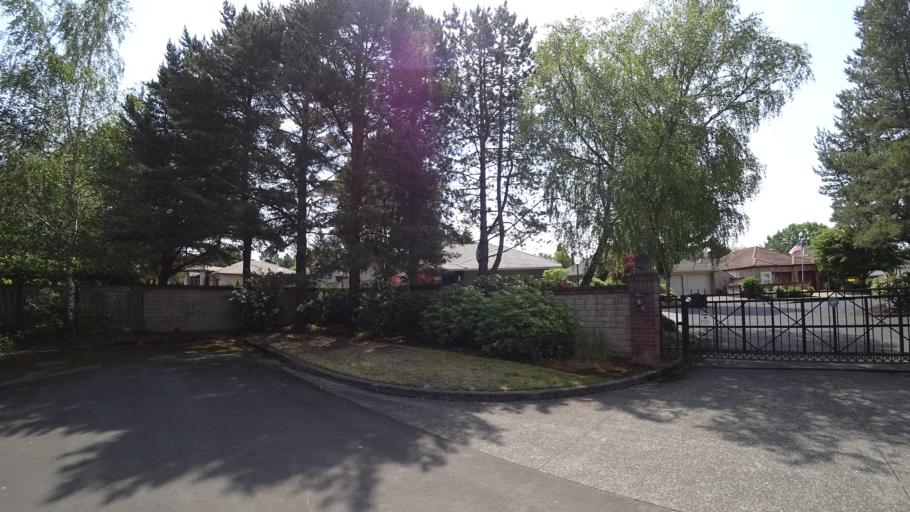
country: US
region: Oregon
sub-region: Washington County
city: Oak Hills
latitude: 45.5446
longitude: -122.8227
